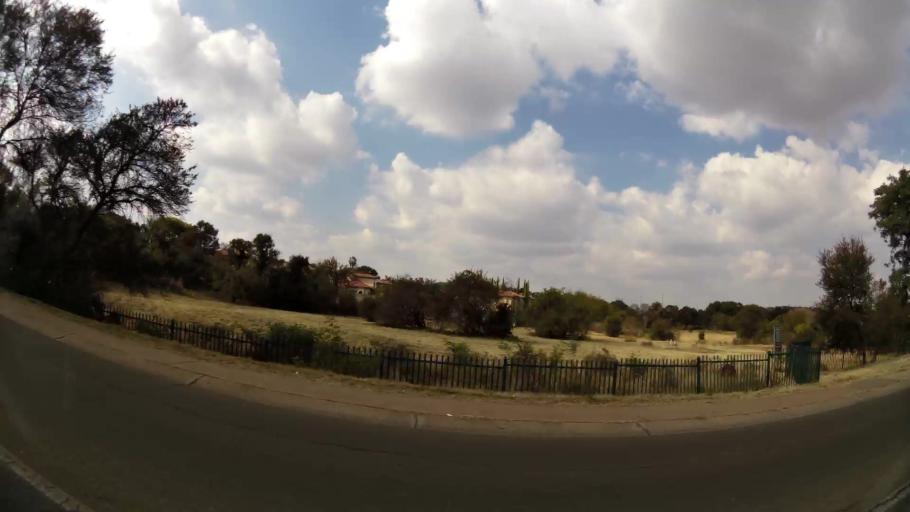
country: ZA
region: Gauteng
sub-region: City of Tshwane Metropolitan Municipality
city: Pretoria
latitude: -25.7804
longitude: 28.3011
